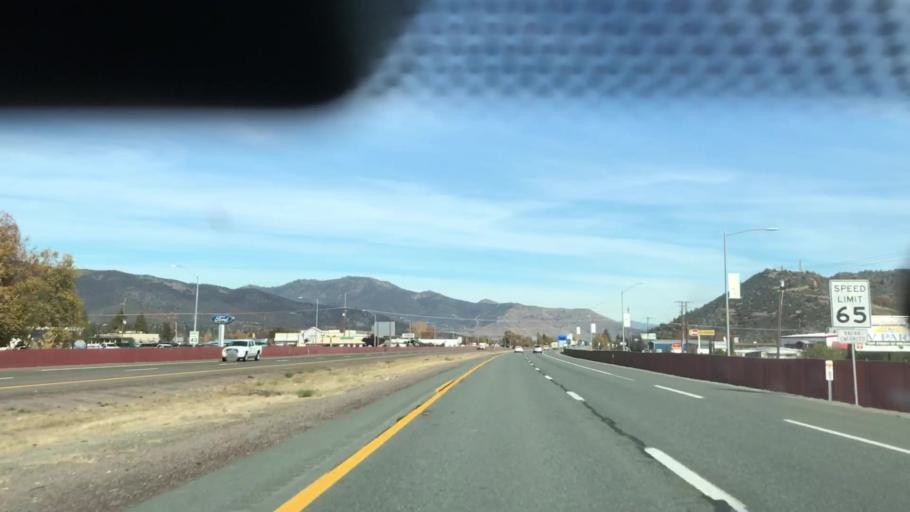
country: US
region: California
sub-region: Siskiyou County
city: Yreka
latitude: 41.7101
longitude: -122.6431
